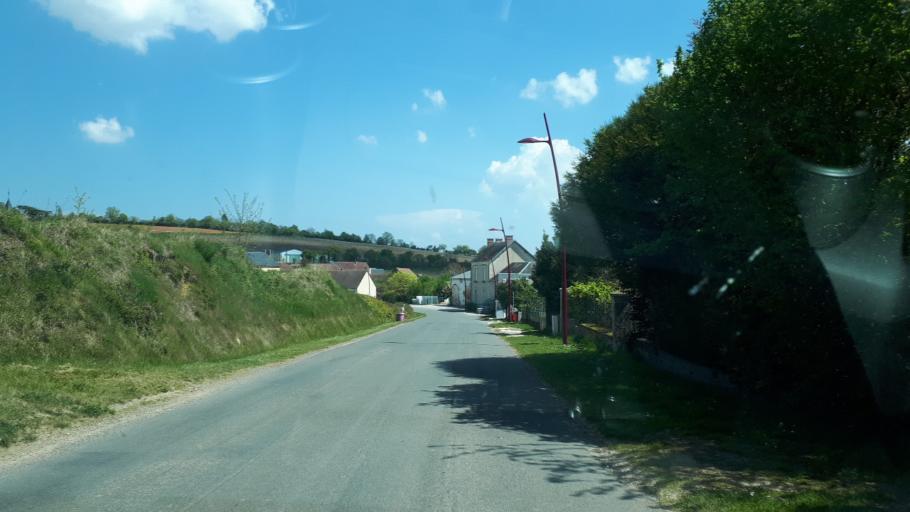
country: FR
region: Centre
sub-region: Departement du Cher
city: Sancerre
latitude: 47.3038
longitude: 2.7414
